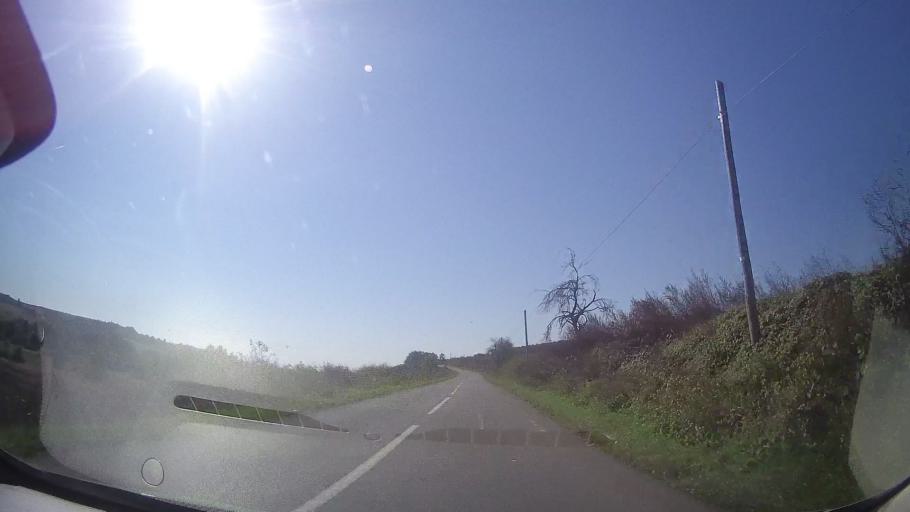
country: RO
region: Timis
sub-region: Comuna Ohaba Lunga
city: Ohaba Lunga
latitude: 45.8949
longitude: 21.9721
